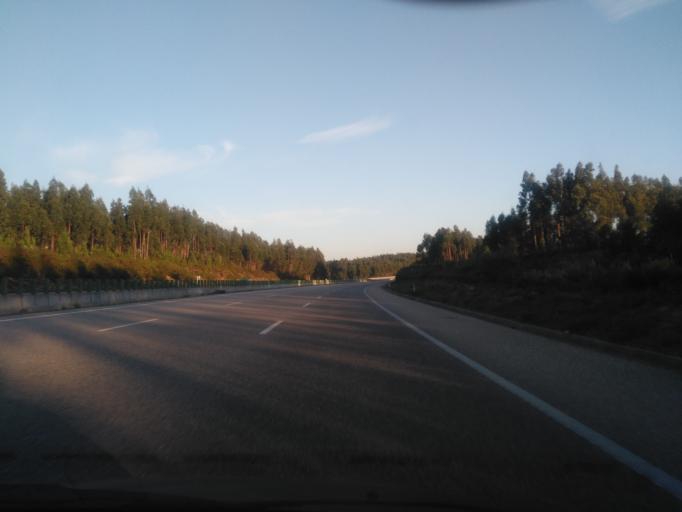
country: PT
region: Leiria
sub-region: Pombal
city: Lourical
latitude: 39.9837
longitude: -8.7879
